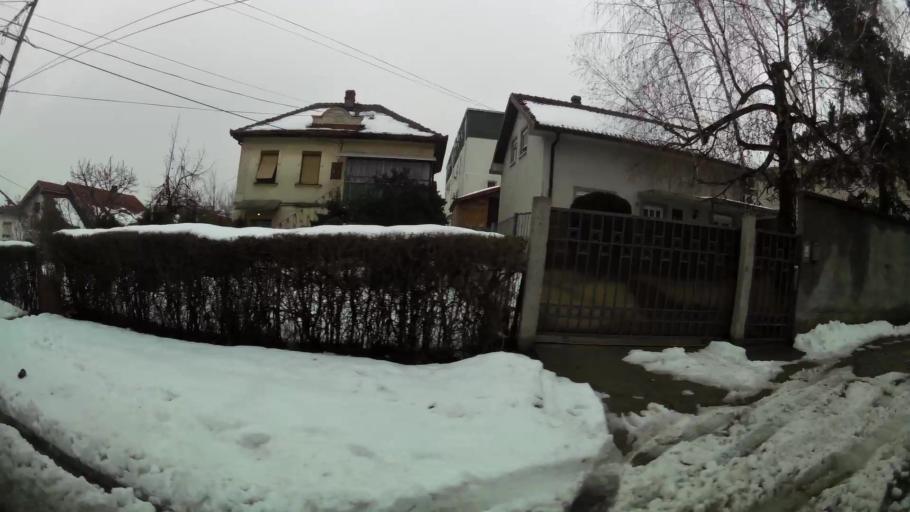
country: RS
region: Central Serbia
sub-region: Belgrade
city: Zvezdara
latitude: 44.7426
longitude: 20.5024
